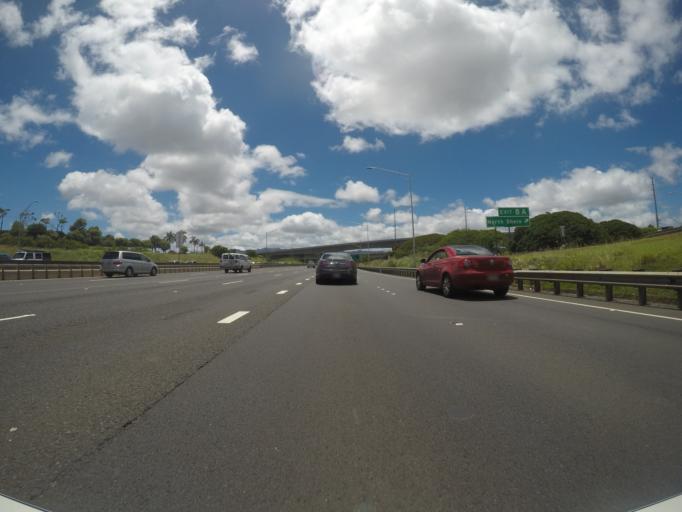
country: US
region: Hawaii
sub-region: Honolulu County
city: Pearl City, Manana
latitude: 21.3948
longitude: -157.9817
